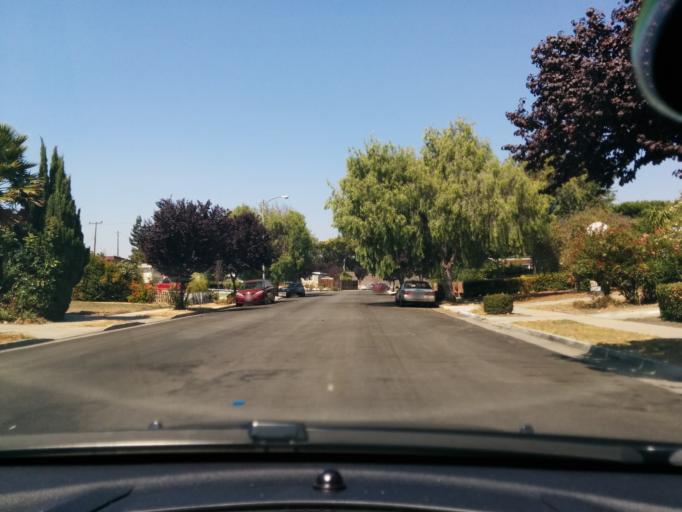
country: US
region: California
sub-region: Santa Clara County
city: Sunnyvale
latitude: 37.3903
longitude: -121.9986
